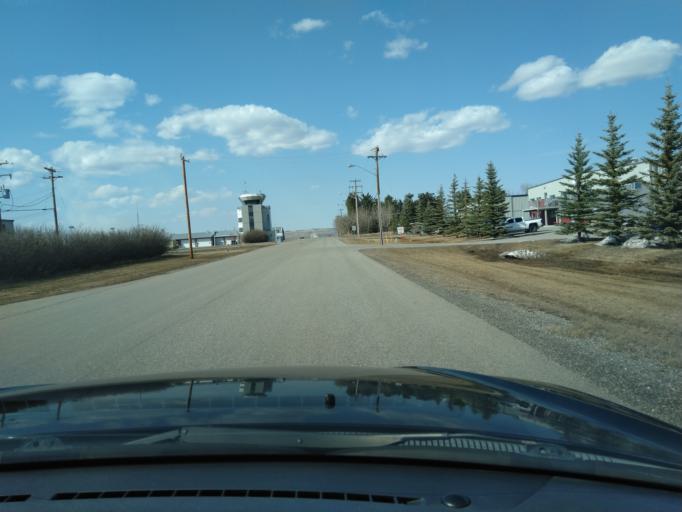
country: CA
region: Alberta
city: Cochrane
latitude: 51.1007
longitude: -114.3737
